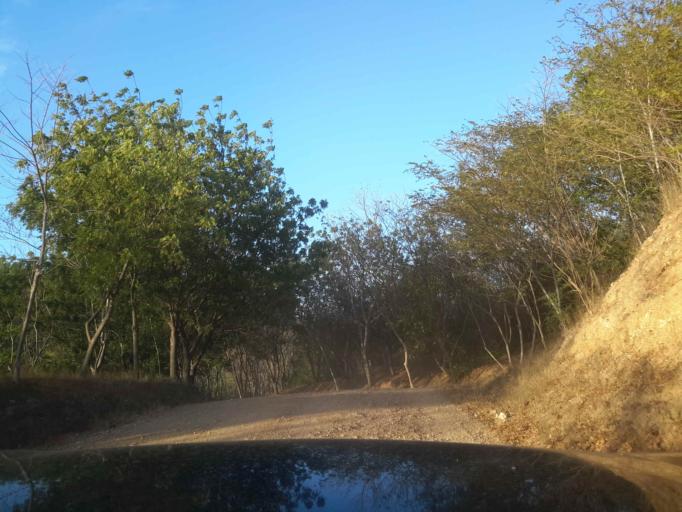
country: NI
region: Rivas
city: San Juan del Sur
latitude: 11.1868
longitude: -85.8132
